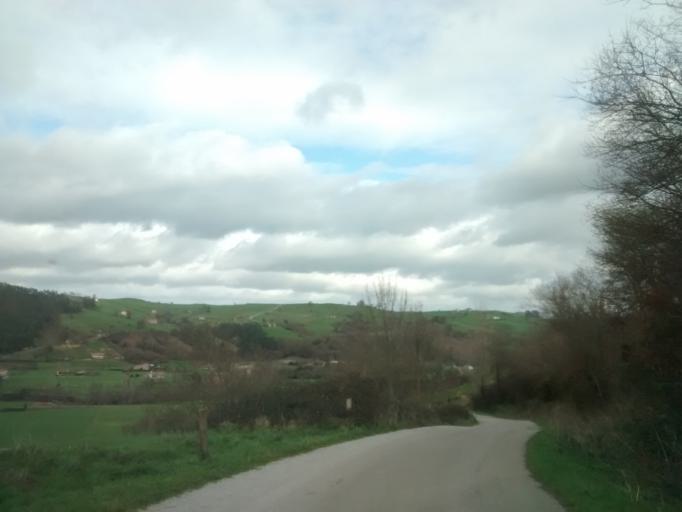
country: ES
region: Cantabria
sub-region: Provincia de Cantabria
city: Lierganes
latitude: 43.3398
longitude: -3.7343
